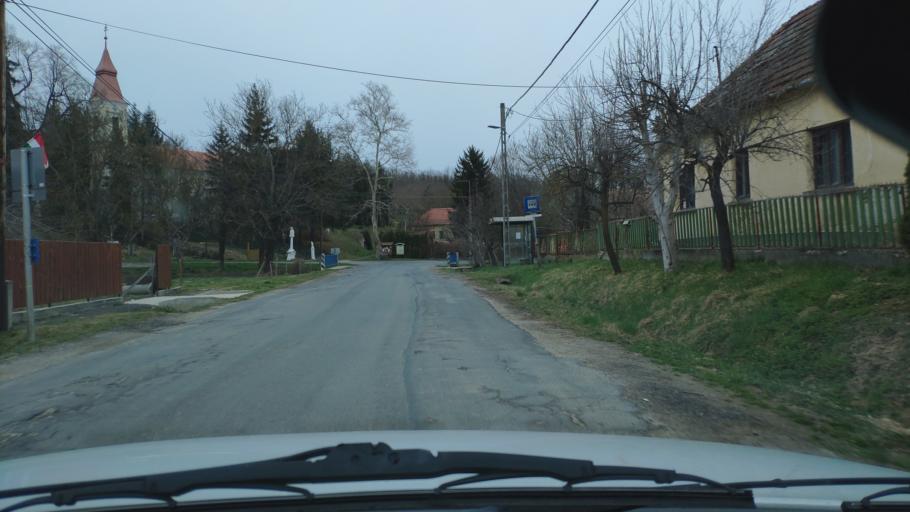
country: HU
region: Zala
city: Pacsa
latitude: 46.6798
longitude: 17.0511
